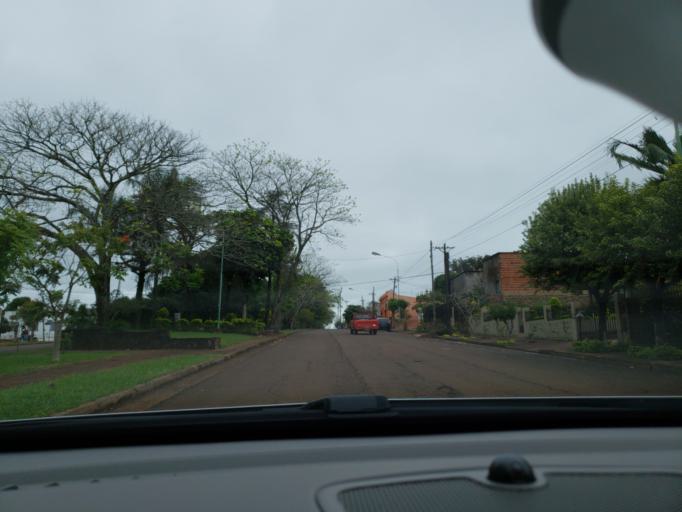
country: AR
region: Misiones
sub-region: Departamento de Apostoles
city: Apostoles
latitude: -27.9080
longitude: -55.7482
